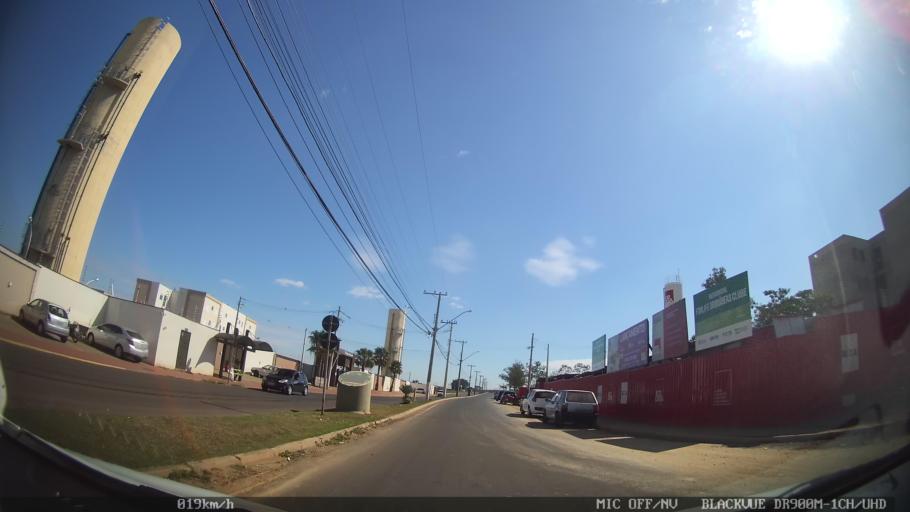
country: BR
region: Sao Paulo
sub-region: Santa Barbara D'Oeste
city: Santa Barbara d'Oeste
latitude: -22.7286
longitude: -47.3982
